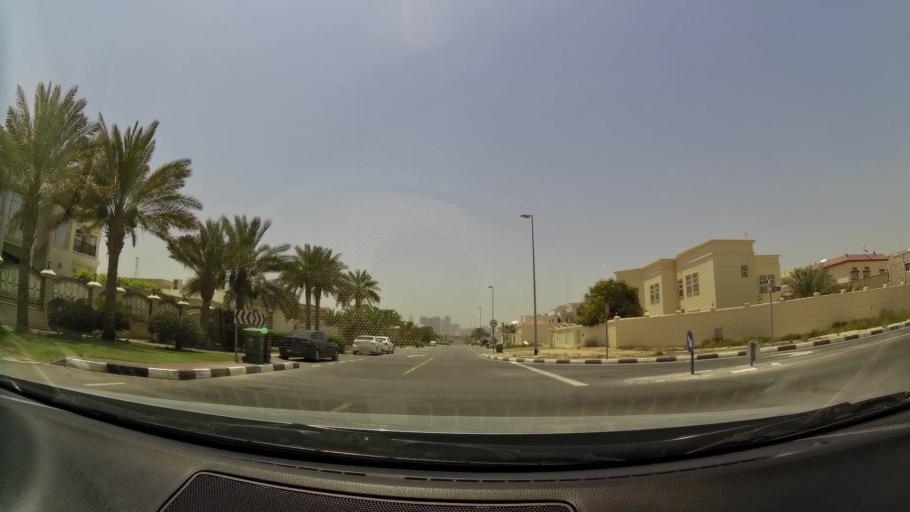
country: AE
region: Dubai
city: Dubai
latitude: 25.0866
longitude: 55.2033
